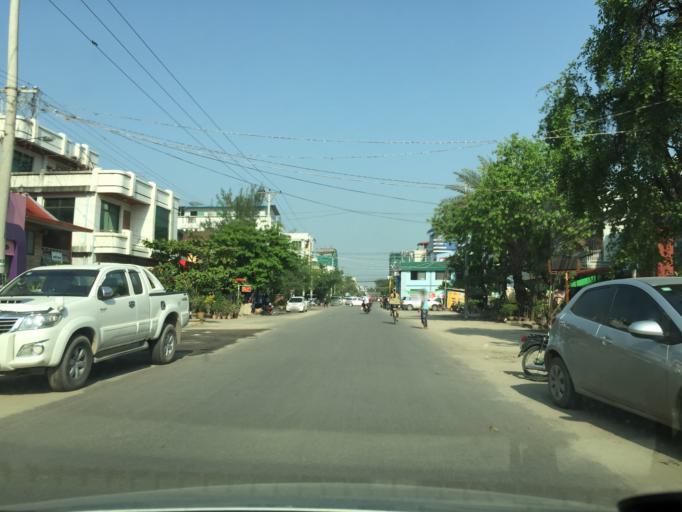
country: MM
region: Mandalay
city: Mandalay
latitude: 21.9735
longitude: 96.0925
